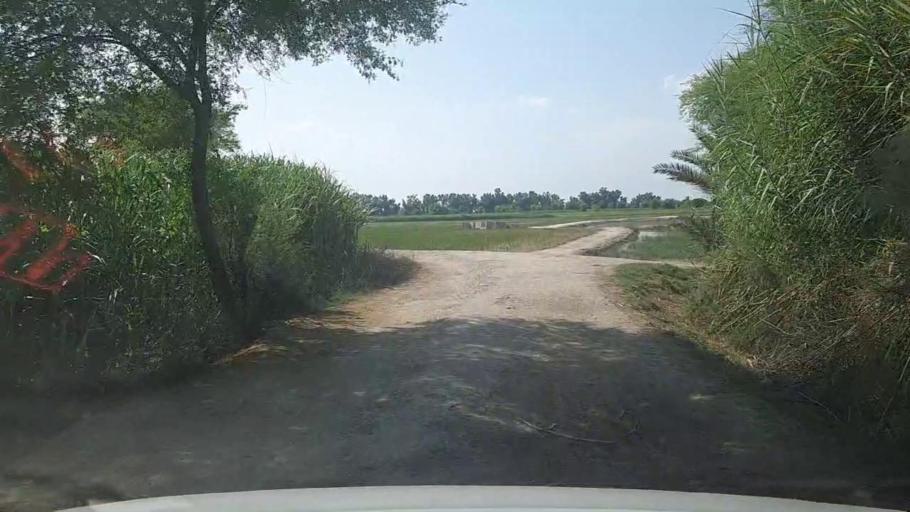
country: PK
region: Sindh
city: Khairpur
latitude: 28.1225
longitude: 69.6052
